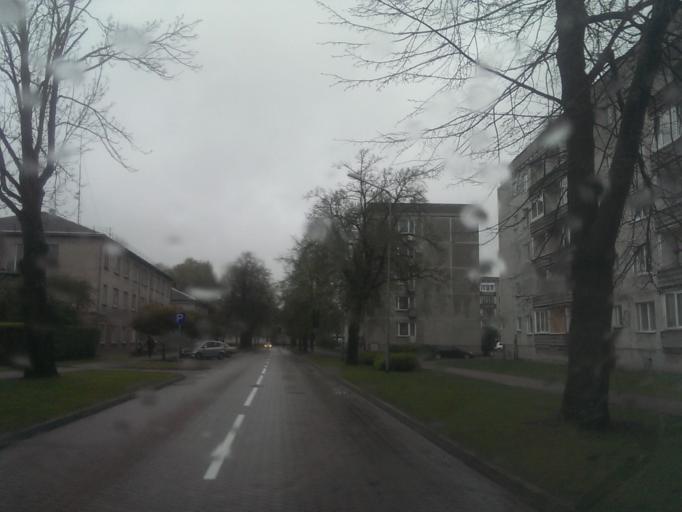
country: LV
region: Ventspils
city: Ventspils
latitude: 57.3914
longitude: 21.5698
